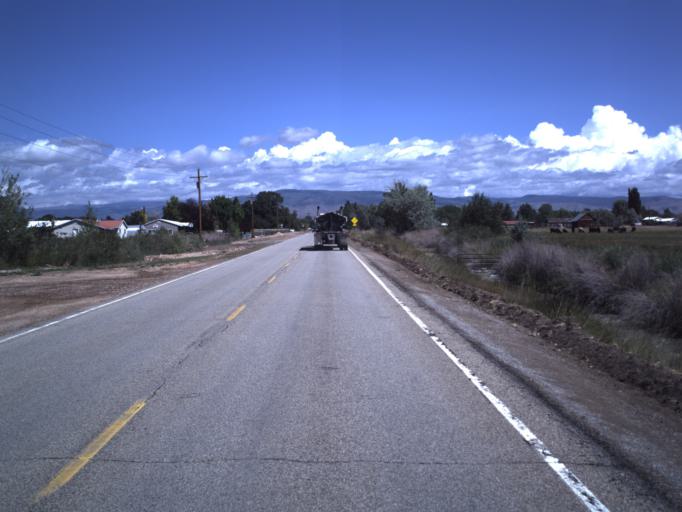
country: US
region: Utah
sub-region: Duchesne County
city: Roosevelt
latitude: 40.4216
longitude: -110.0300
